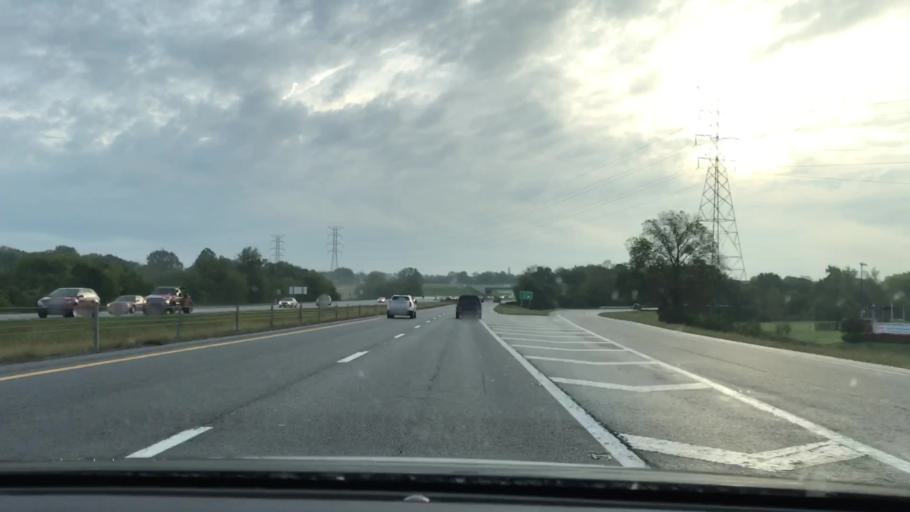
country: US
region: Tennessee
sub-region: Sumner County
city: Hendersonville
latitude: 36.3328
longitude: -86.6001
